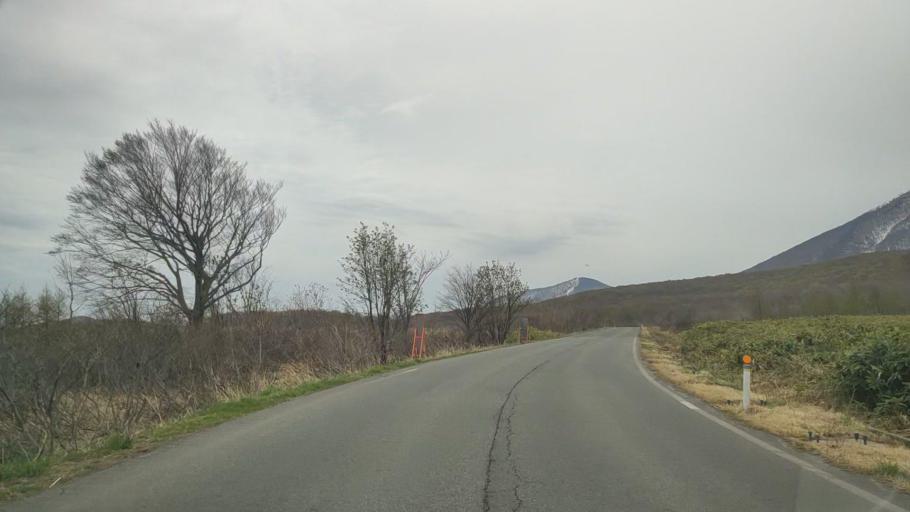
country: JP
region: Aomori
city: Aomori Shi
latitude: 40.6880
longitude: 140.9244
